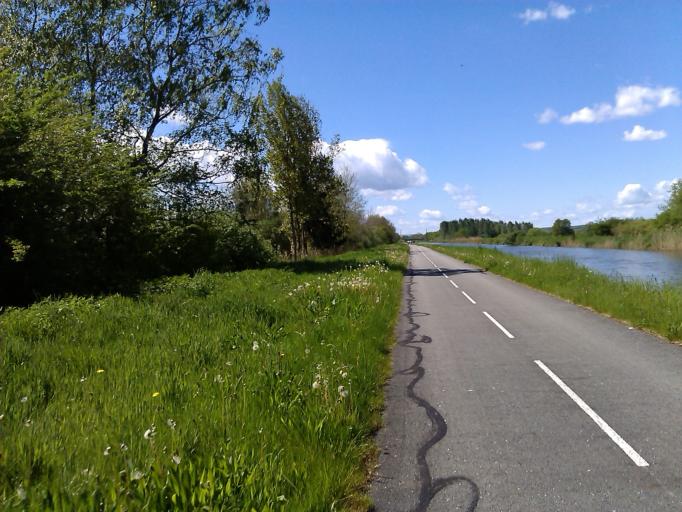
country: FR
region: Franche-Comte
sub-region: Territoire de Belfort
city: Montreux-Chateau
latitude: 47.5886
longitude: 6.9761
